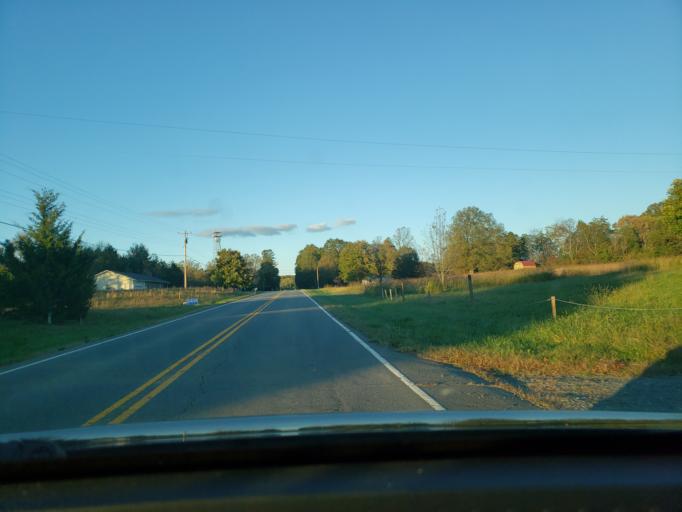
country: US
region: North Carolina
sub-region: Stokes County
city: Danbury
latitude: 36.3338
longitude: -80.2236
